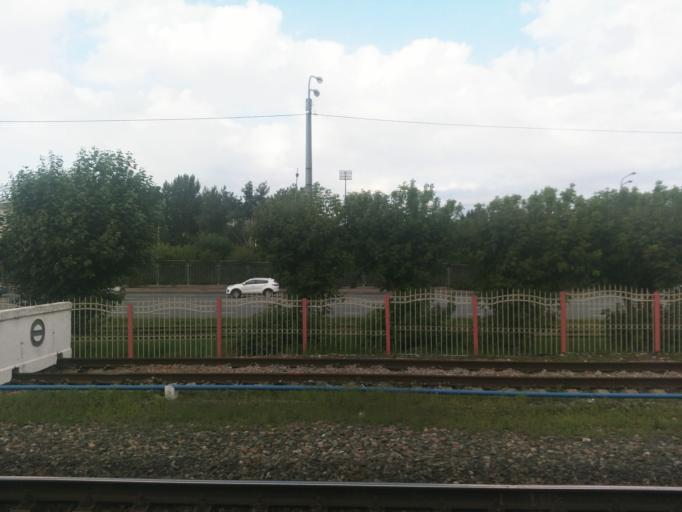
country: RU
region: Tatarstan
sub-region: Gorod Kazan'
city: Kazan
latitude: 55.7944
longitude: 49.0945
